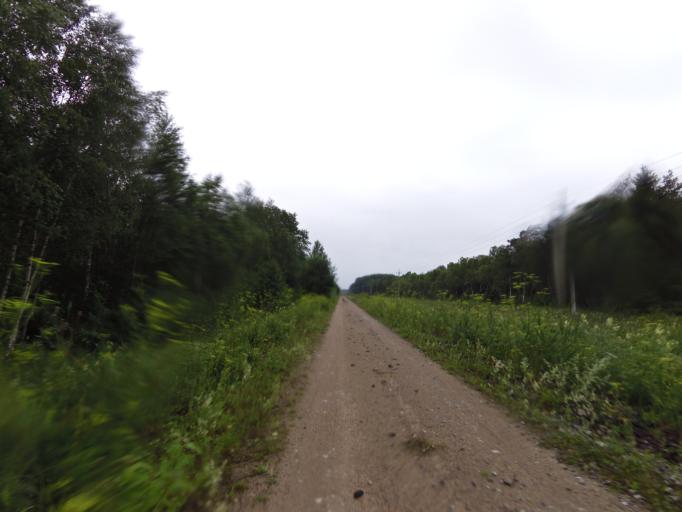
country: EE
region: Laeaene
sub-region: Lihula vald
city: Lihula
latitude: 58.9844
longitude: 23.9265
